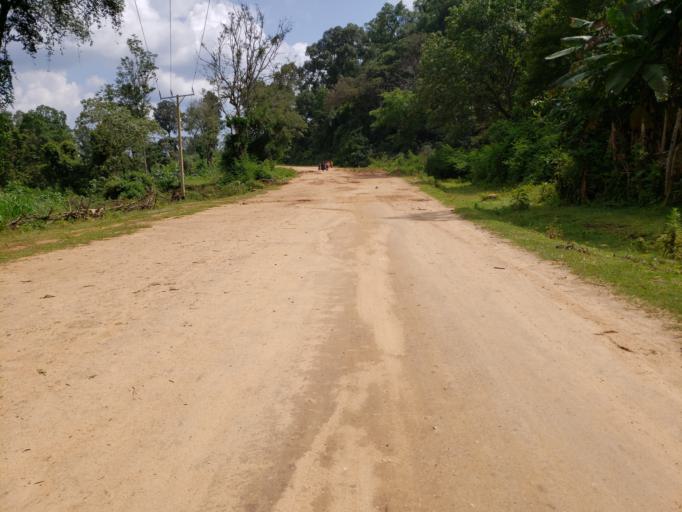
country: ET
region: Oromiya
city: Dodola
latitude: 6.4510
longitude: 39.5697
